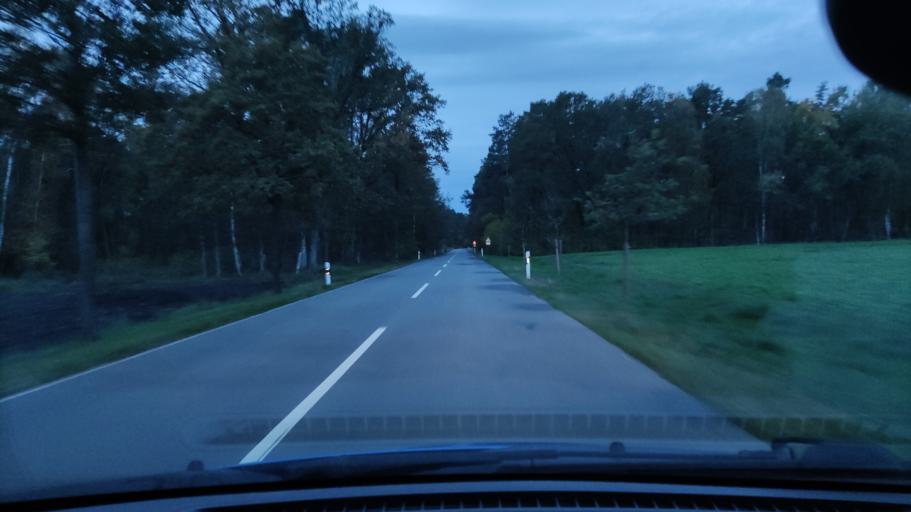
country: DE
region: Lower Saxony
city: Prezelle
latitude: 52.9614
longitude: 11.3836
